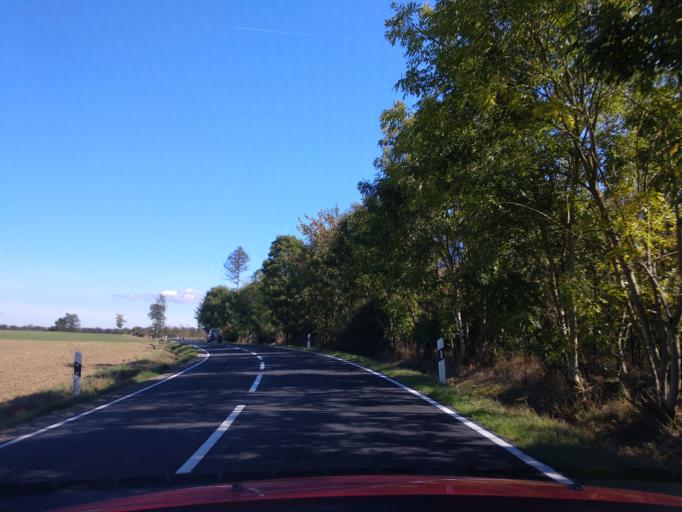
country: DE
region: Lower Saxony
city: Boffzen
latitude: 51.7315
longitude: 9.2933
